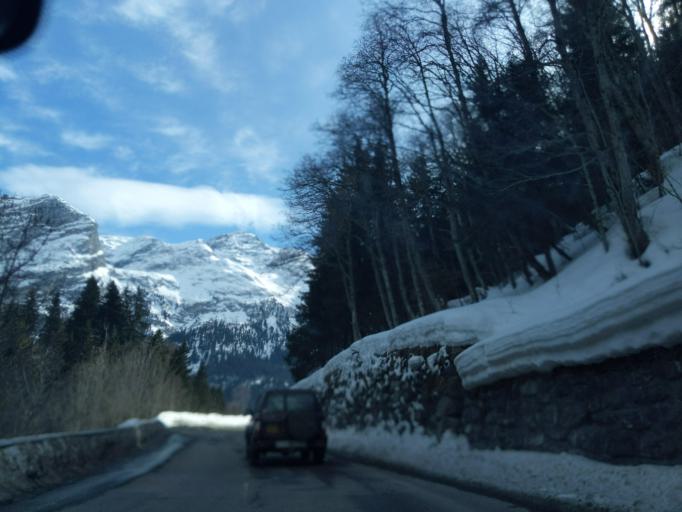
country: FR
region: Rhone-Alpes
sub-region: Departement de la Savoie
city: Courchevel
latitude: 45.3890
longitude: 6.7128
